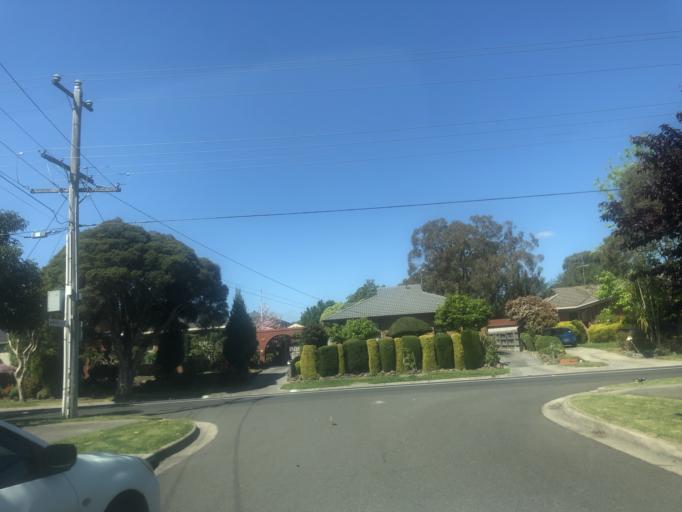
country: AU
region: Victoria
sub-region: Monash
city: Notting Hill
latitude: -37.9030
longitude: 145.1729
